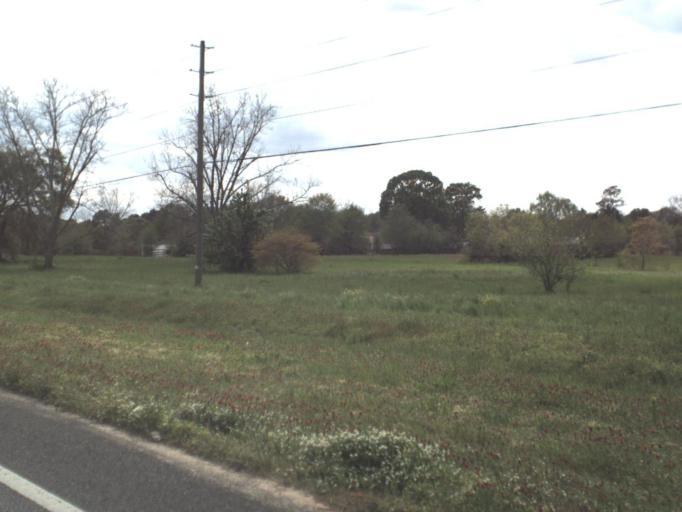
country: US
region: Florida
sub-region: Okaloosa County
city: Crestview
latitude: 30.8176
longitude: -86.5388
